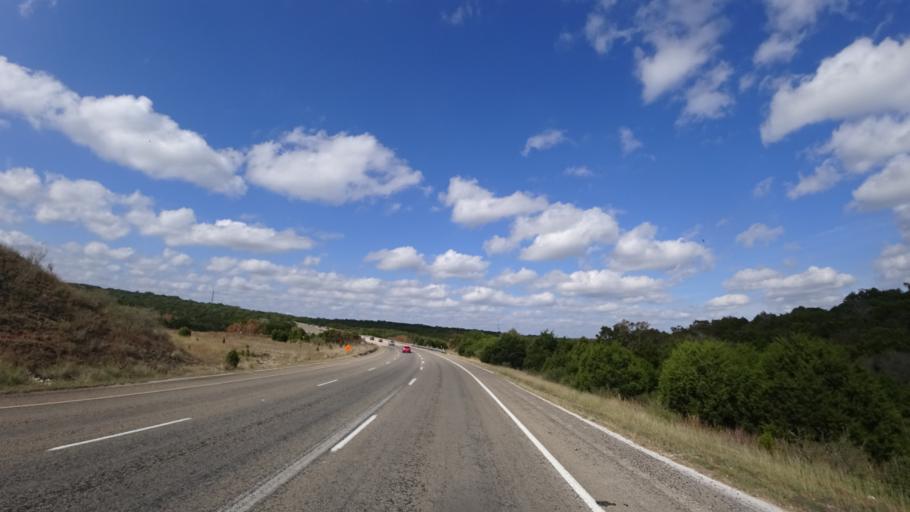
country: US
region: Texas
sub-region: Travis County
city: Barton Creek
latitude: 30.2785
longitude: -97.8992
